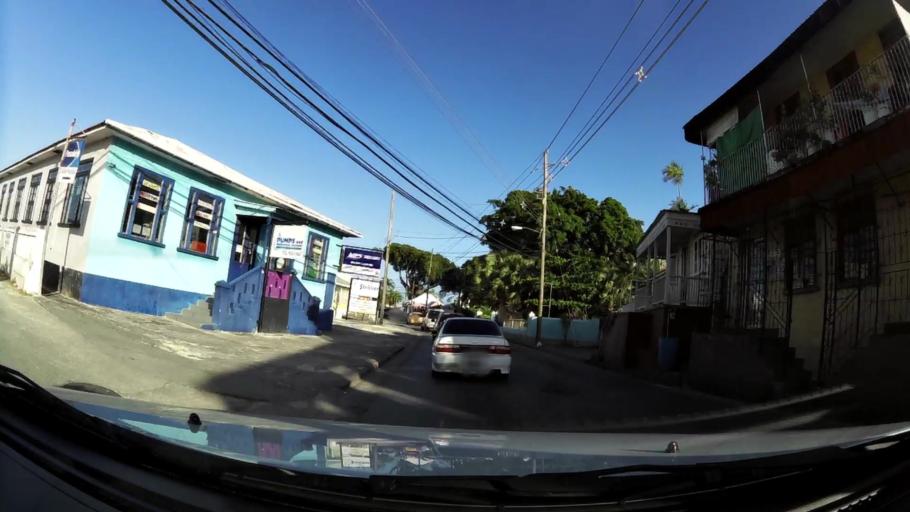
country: BB
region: Saint Michael
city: Bridgetown
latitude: 13.0843
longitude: -59.6082
